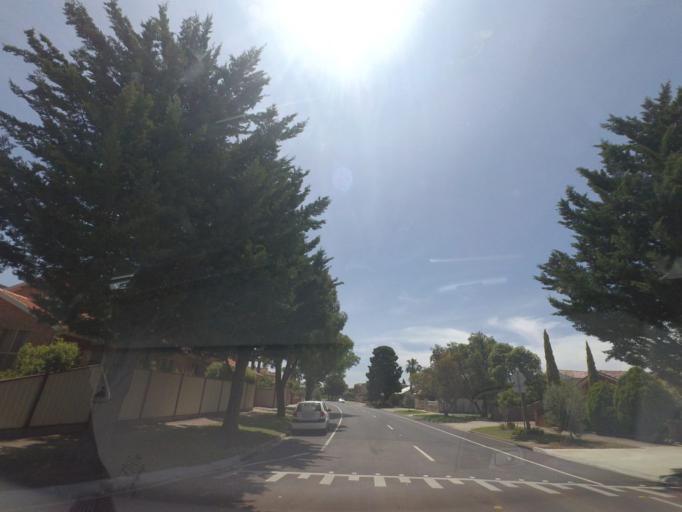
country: AU
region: Victoria
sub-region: Brimbank
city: Keilor Downs
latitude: -37.7189
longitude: 144.8029
